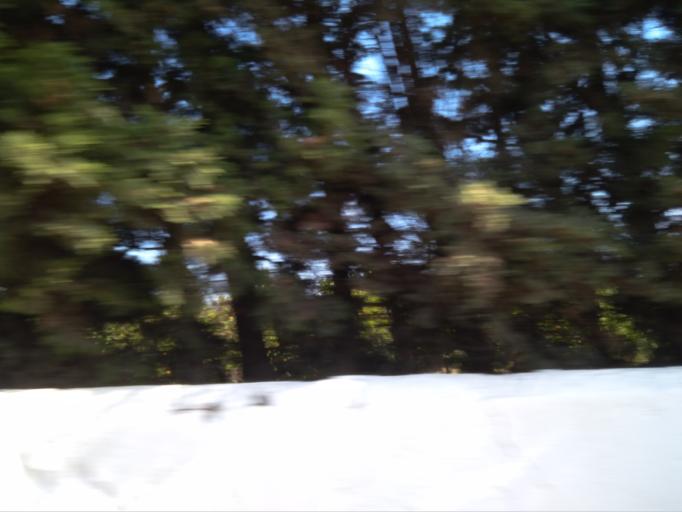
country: PT
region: Faro
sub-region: Faro
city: Santa Barbara de Nexe
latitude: 37.0659
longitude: -7.9557
